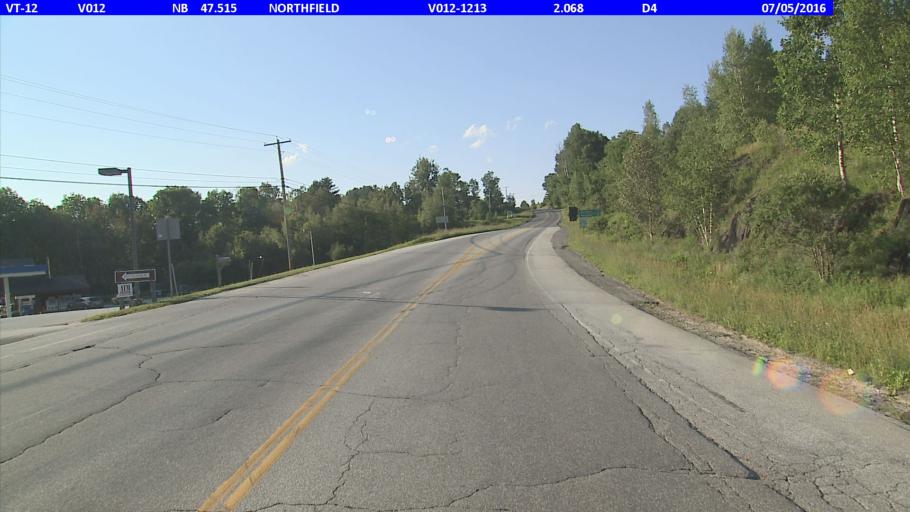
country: US
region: Vermont
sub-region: Washington County
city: Northfield
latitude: 44.1190
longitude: -72.6562
